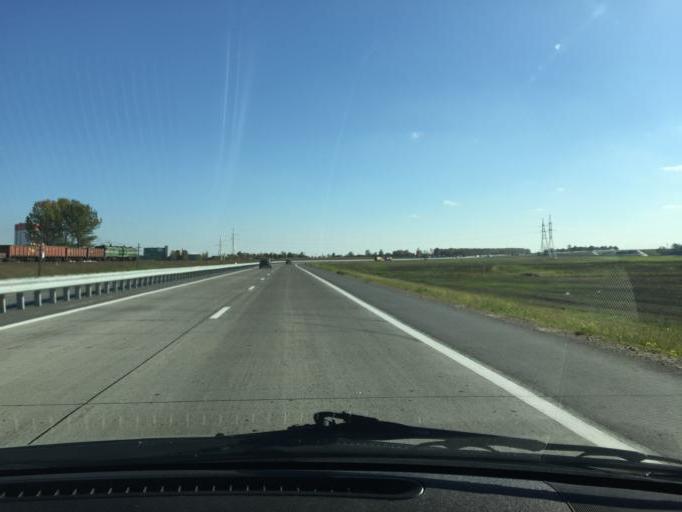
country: BY
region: Minsk
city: Slutsk
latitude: 53.0001
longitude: 27.5010
